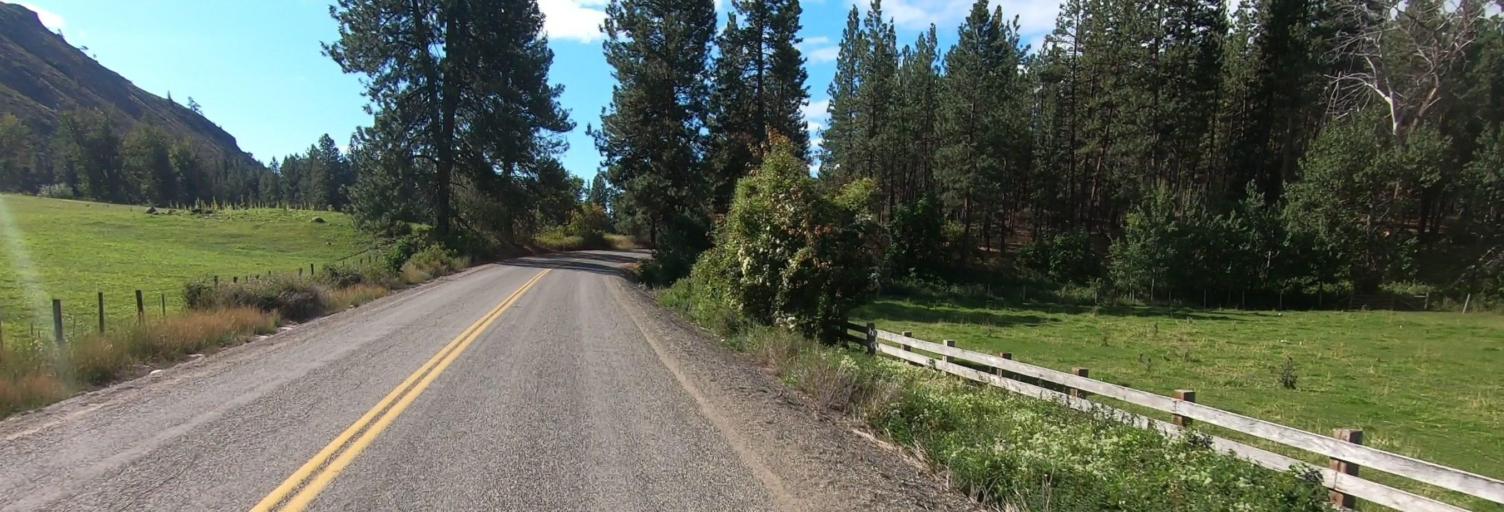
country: US
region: Washington
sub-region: Okanogan County
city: Brewster
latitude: 48.5450
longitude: -120.1787
